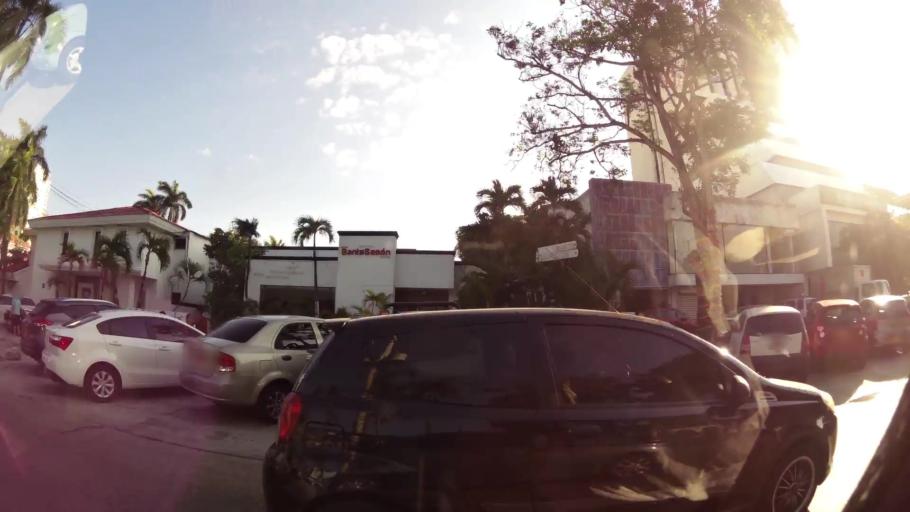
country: CO
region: Atlantico
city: Barranquilla
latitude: 10.9999
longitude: -74.8049
